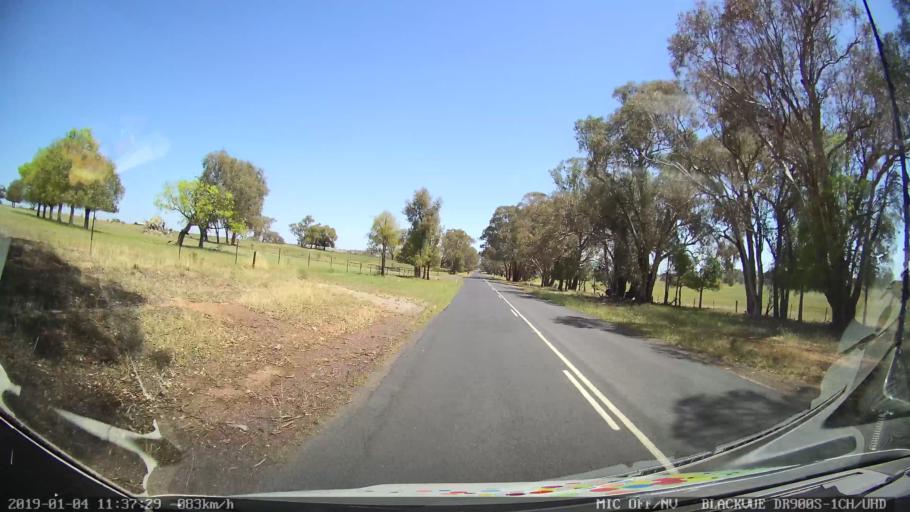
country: AU
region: New South Wales
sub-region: Cabonne
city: Molong
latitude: -33.0318
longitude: 148.8070
